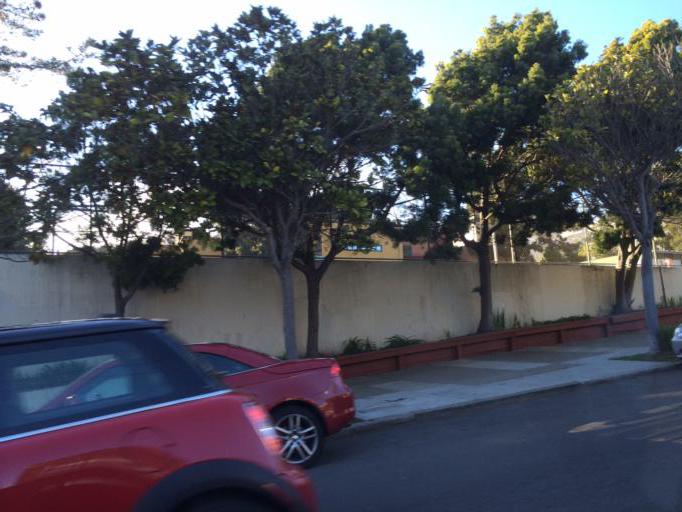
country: US
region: California
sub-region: San Francisco County
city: San Francisco
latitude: 37.7667
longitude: -122.4356
